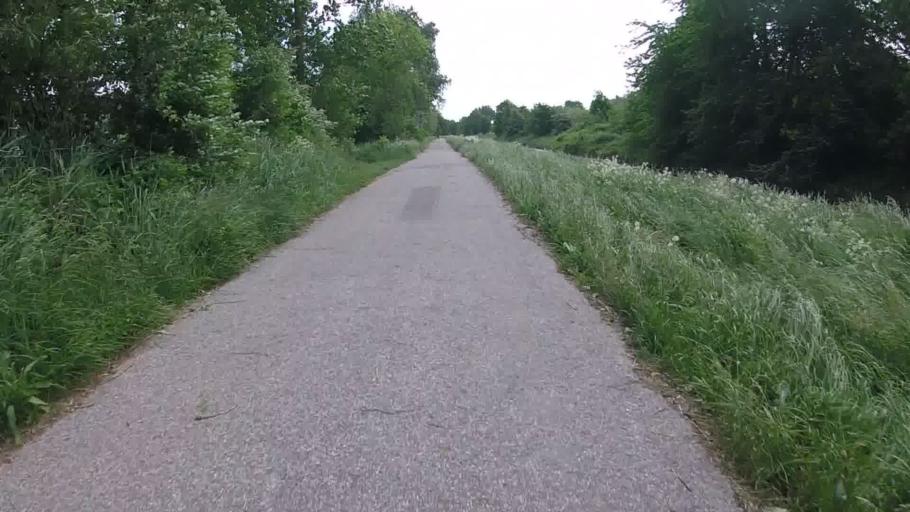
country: DE
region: Schleswig-Holstein
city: Oststeinbek
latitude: 53.4933
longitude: 10.1454
